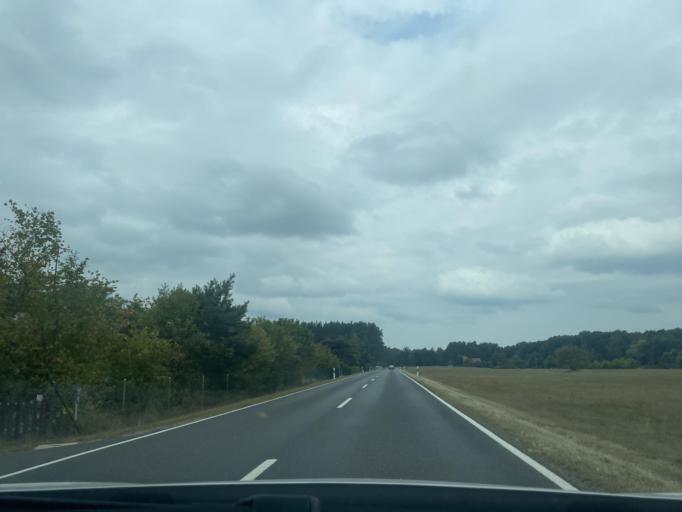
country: DE
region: Saxony
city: Mucka
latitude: 51.2818
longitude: 14.6933
